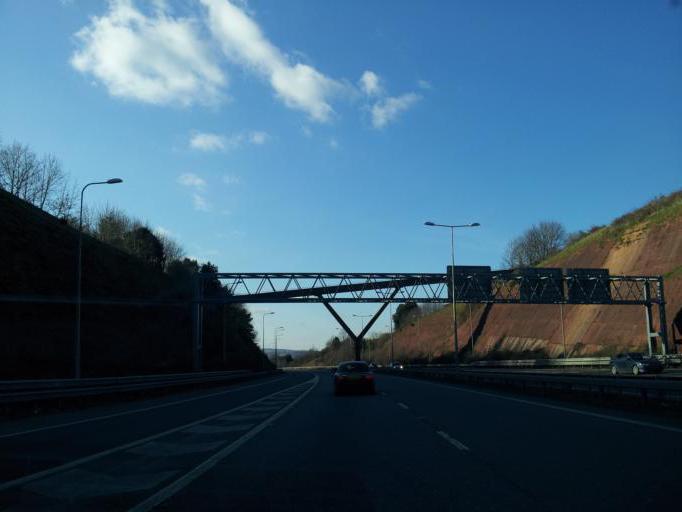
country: GB
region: England
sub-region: Devon
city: Exminster
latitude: 50.6814
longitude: -3.5182
